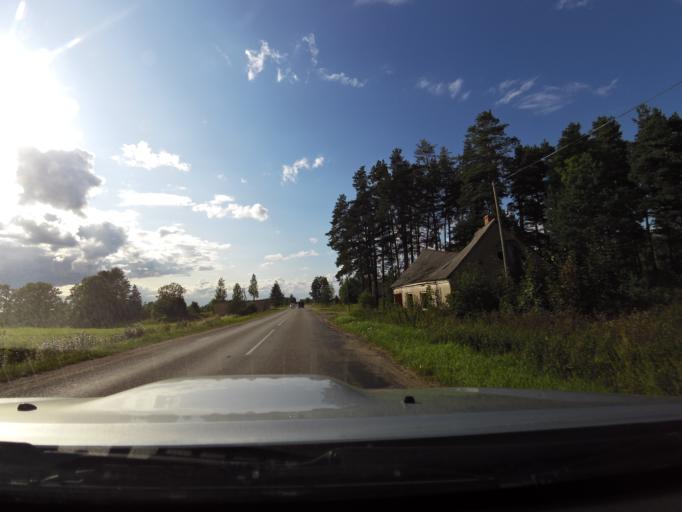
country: LV
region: Akniste
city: Akniste
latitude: 56.1456
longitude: 25.7951
